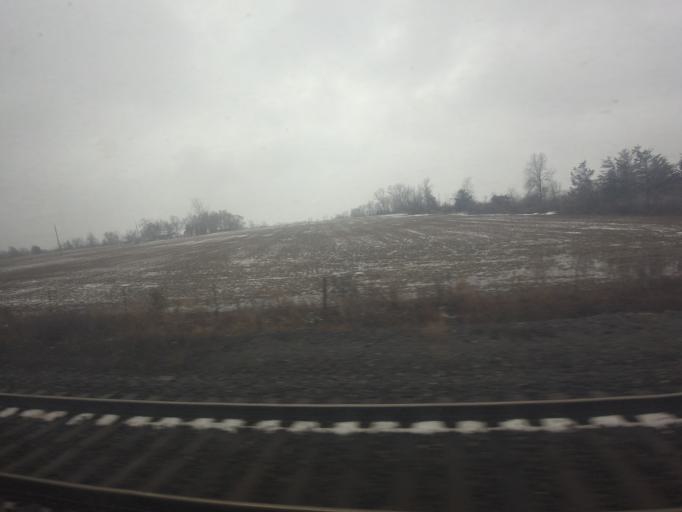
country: CA
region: Ontario
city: Belleville
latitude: 44.2044
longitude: -77.2716
